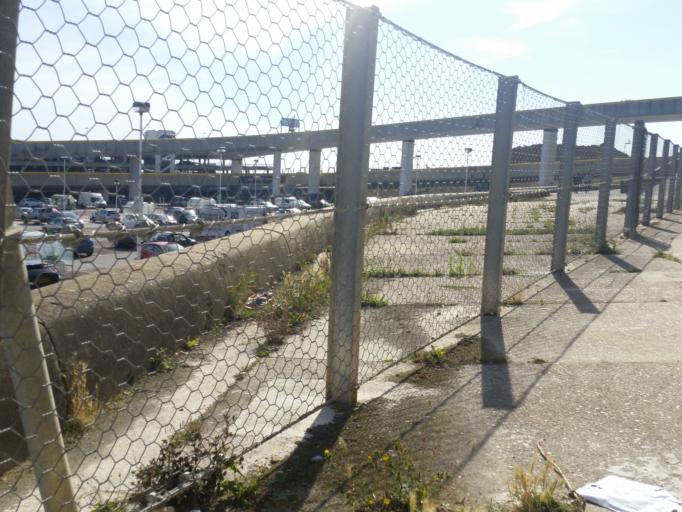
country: GB
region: England
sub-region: Brighton and Hove
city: Brighton
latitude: 50.8144
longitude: -0.1049
